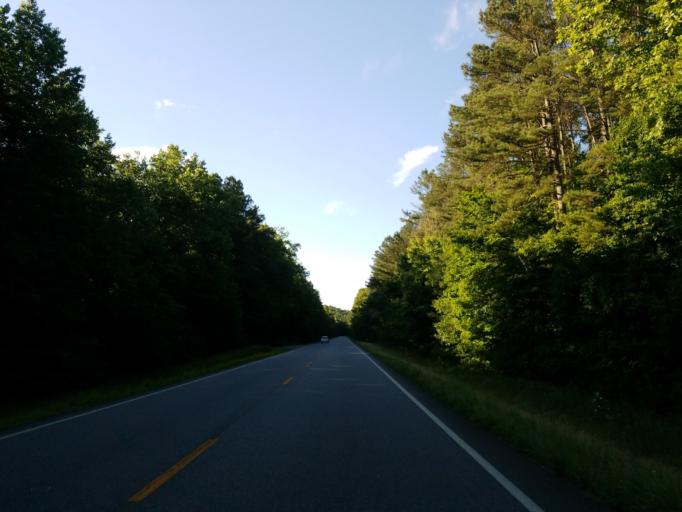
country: US
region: Georgia
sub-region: Whitfield County
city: Dalton
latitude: 34.6464
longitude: -85.0611
